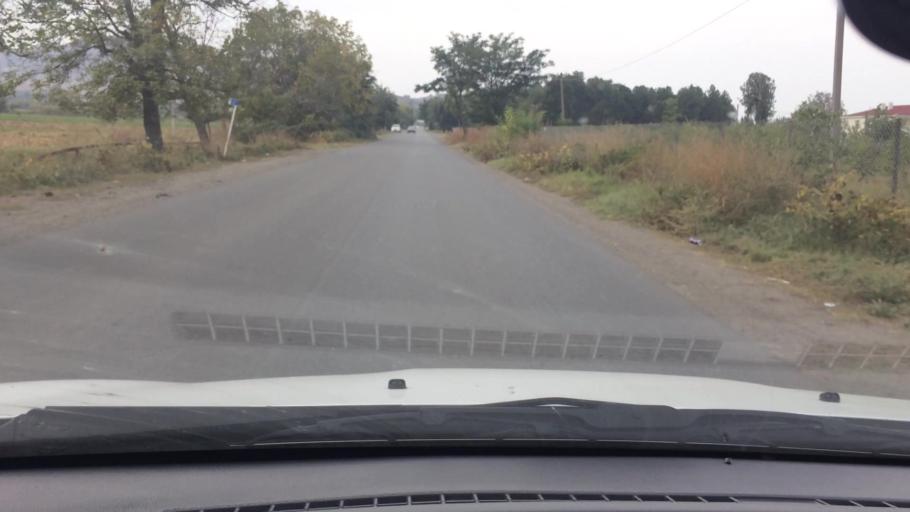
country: GE
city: Naghvarevi
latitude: 41.3567
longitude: 44.8548
